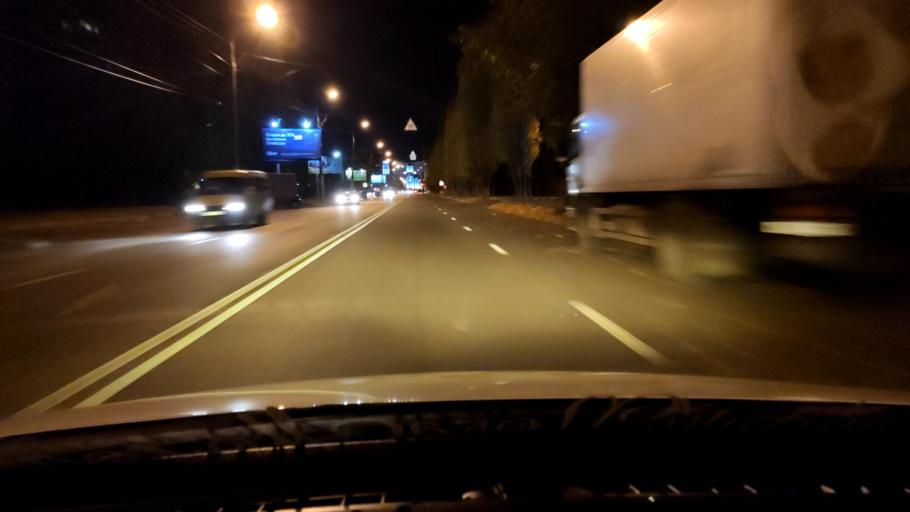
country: RU
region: Voronezj
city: Podgornoye
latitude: 51.7092
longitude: 39.1739
